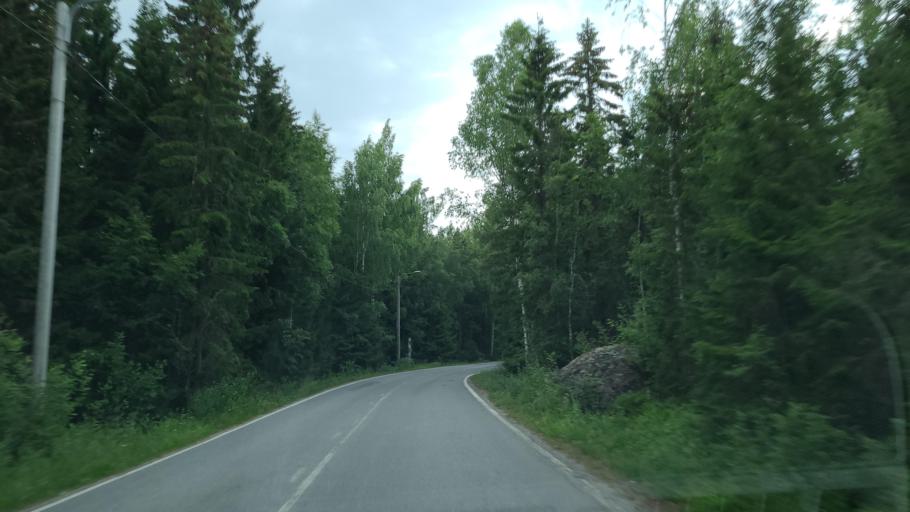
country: FI
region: Ostrobothnia
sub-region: Vaasa
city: Replot
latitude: 63.1752
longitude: 21.2765
